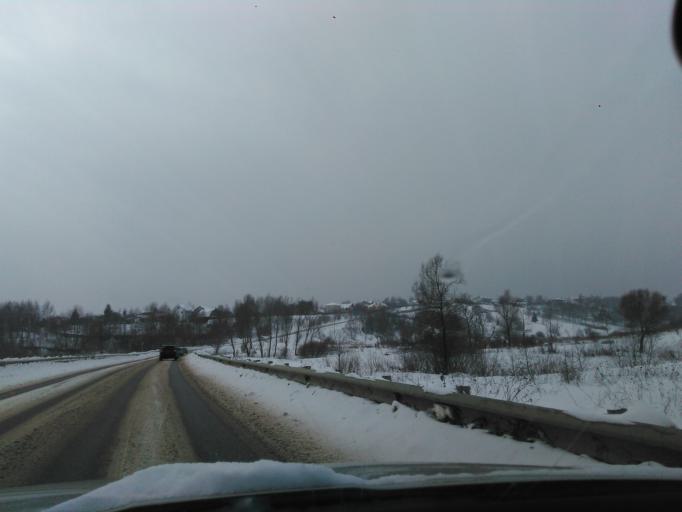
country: RU
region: Moskovskaya
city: Yakhroma
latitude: 56.2702
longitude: 37.4891
